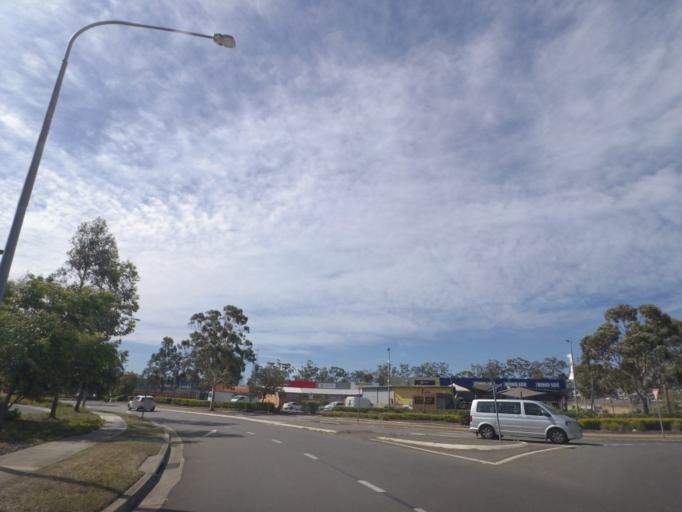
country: AU
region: New South Wales
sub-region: Campbelltown Municipality
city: Glenfield
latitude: -33.9592
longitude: 150.8813
